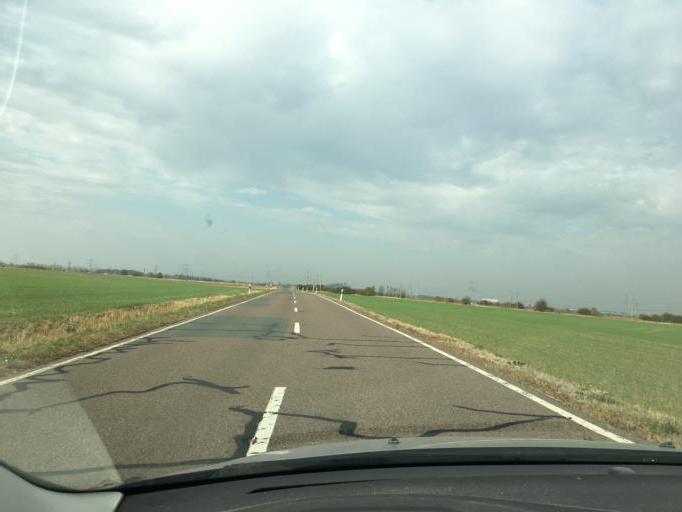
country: DE
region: Saxony
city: Wiedemar
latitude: 51.5026
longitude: 12.1965
